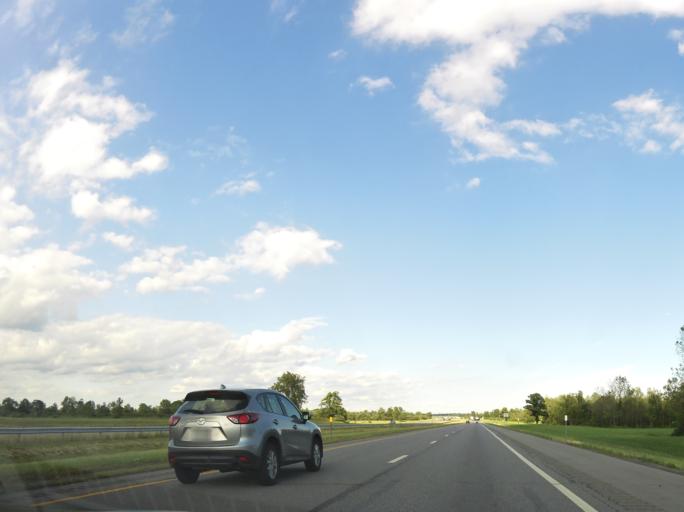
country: US
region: New York
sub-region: Erie County
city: Harris Hill
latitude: 42.9474
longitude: -78.6507
